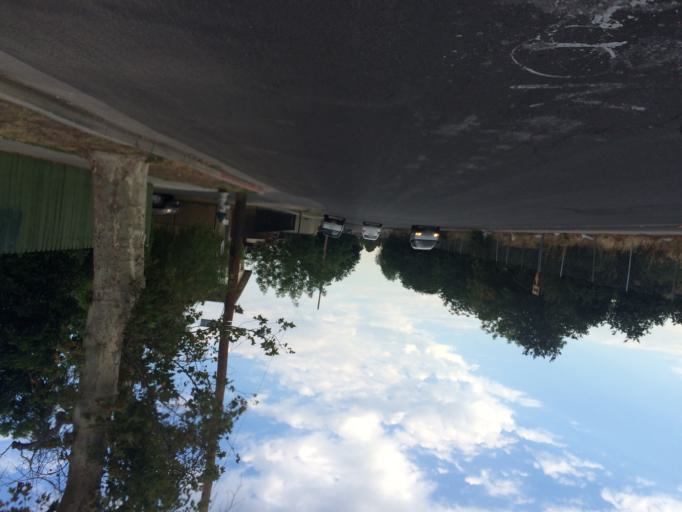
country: US
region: California
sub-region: Fresno County
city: Fresno
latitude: 36.7490
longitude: -119.7771
